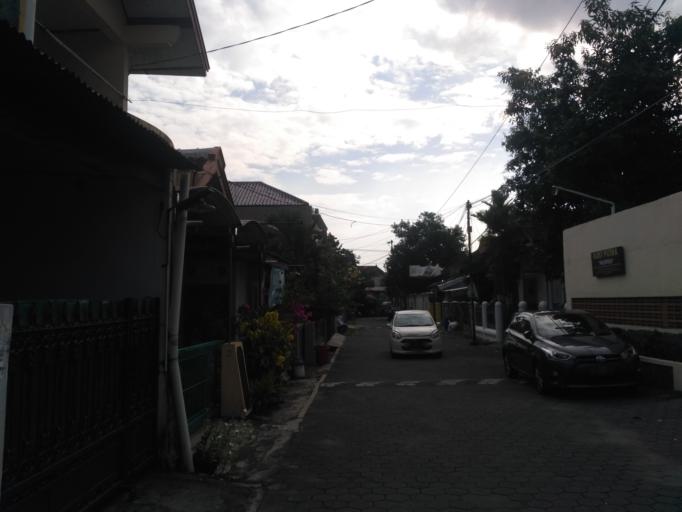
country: ID
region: Daerah Istimewa Yogyakarta
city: Depok
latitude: -7.7670
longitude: 110.4064
